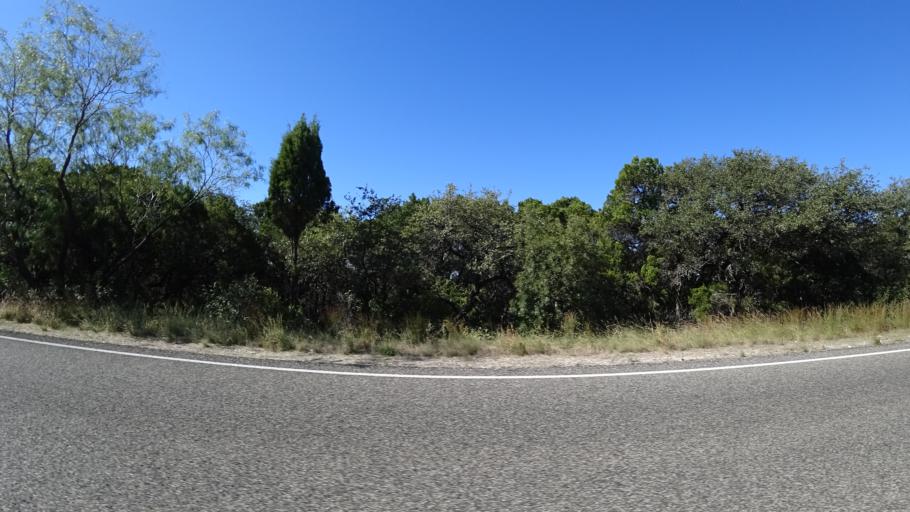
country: US
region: Texas
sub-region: Travis County
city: West Lake Hills
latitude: 30.3438
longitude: -97.7850
